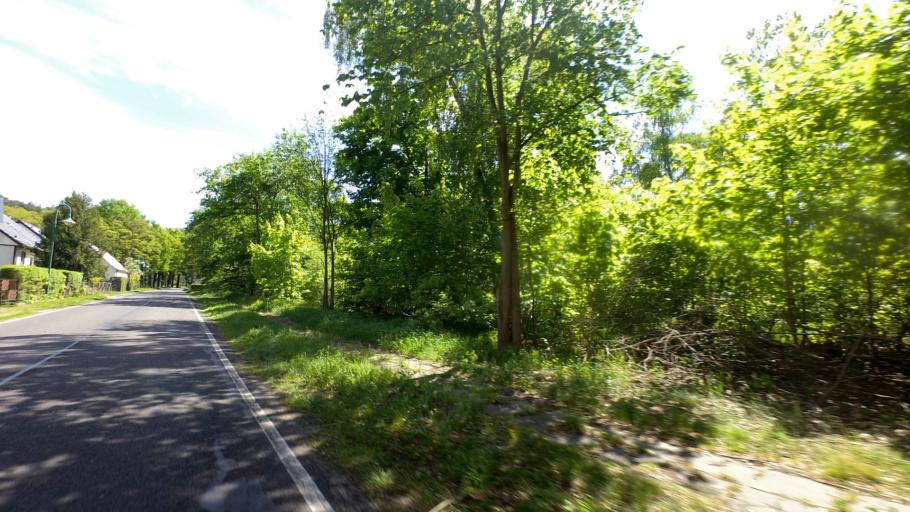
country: DE
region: Brandenburg
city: Baruth
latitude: 52.0502
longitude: 13.4360
